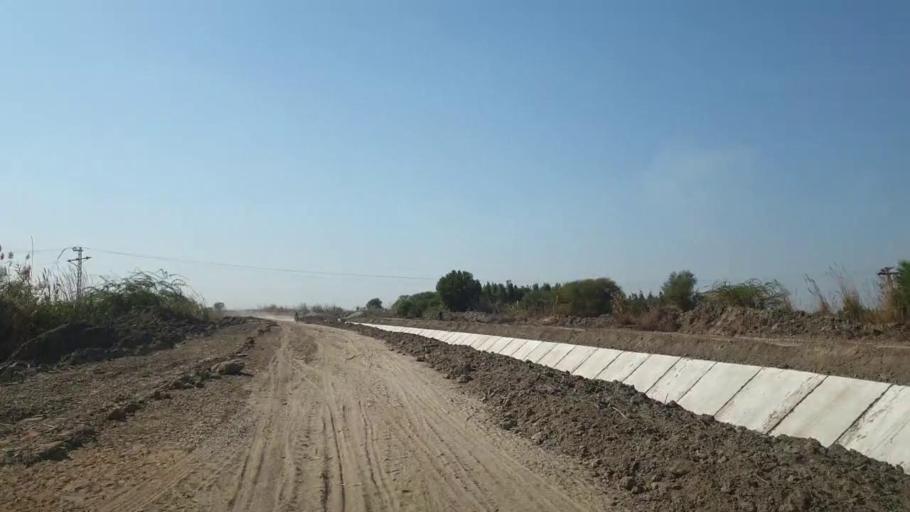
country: PK
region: Sindh
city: Mirpur Khas
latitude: 25.6503
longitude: 69.0077
